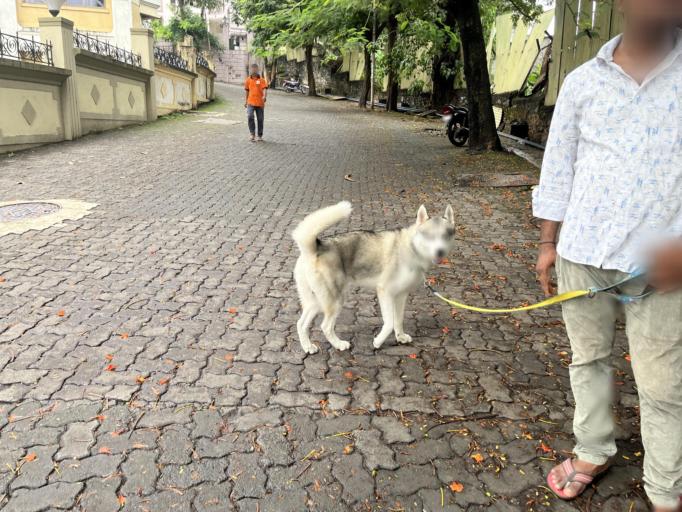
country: IN
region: Maharashtra
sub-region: Mumbai Suburban
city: Borivli
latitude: 19.2273
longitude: 72.8650
